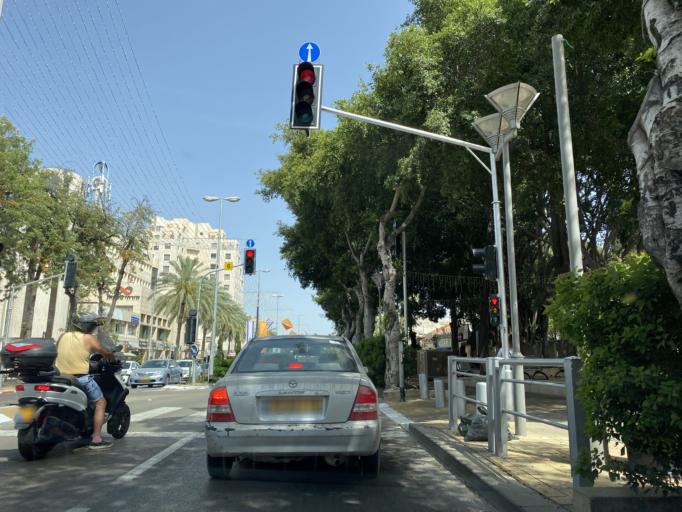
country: IL
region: Central District
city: Ra'anana
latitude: 32.1800
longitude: 34.8766
